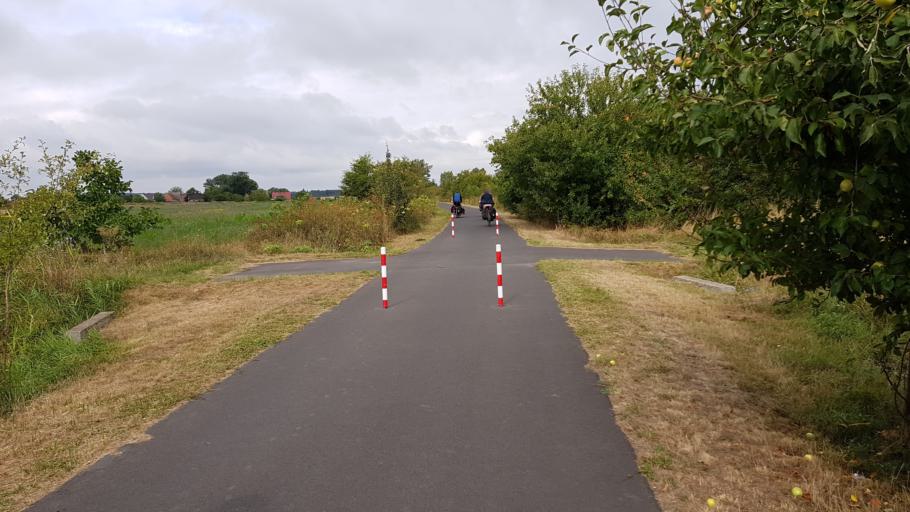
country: PL
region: West Pomeranian Voivodeship
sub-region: Powiat pyrzycki
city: Przelewice
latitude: 53.1331
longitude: 15.0154
